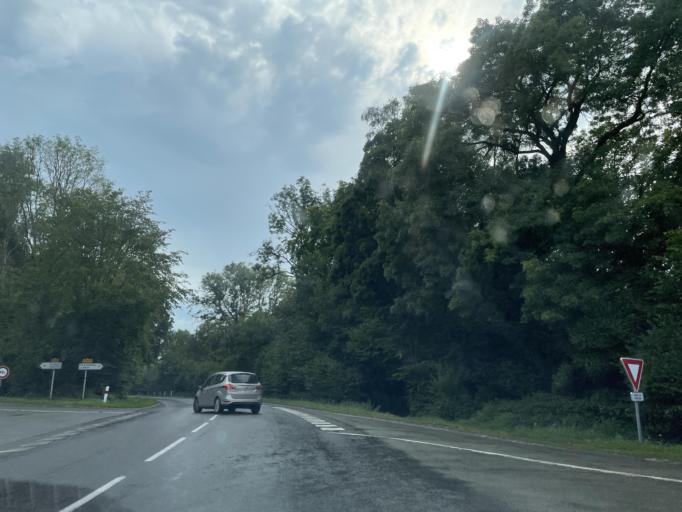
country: FR
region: Haute-Normandie
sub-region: Departement de la Seine-Maritime
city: Neufchatel-en-Bray
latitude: 49.7631
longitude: 1.4264
